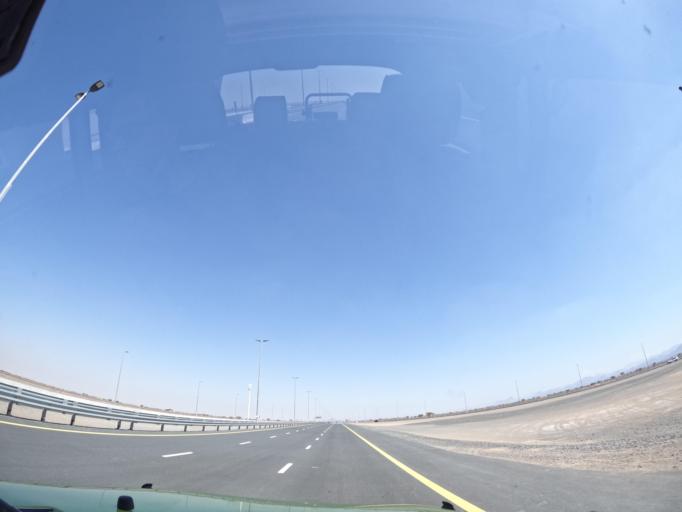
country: AE
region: Ash Shariqah
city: Adh Dhayd
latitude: 25.0725
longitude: 55.9098
